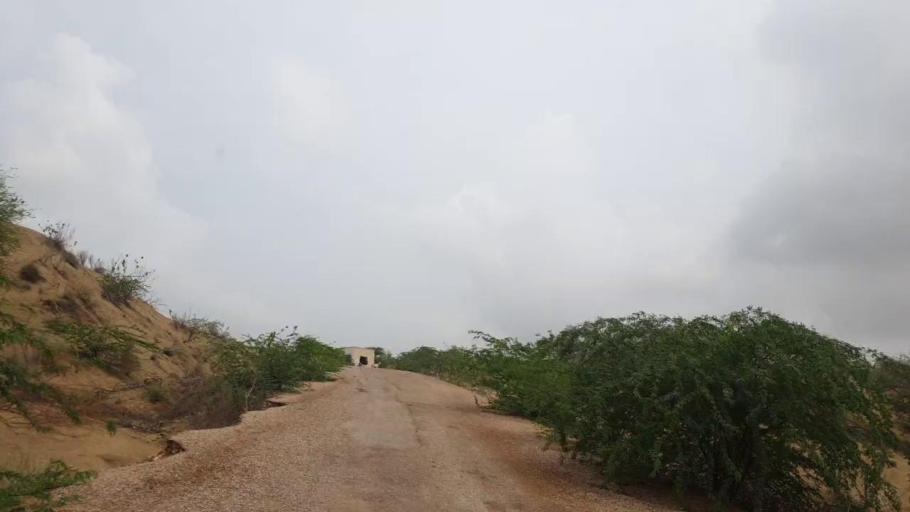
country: PK
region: Sindh
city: Diplo
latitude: 24.5580
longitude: 69.4549
